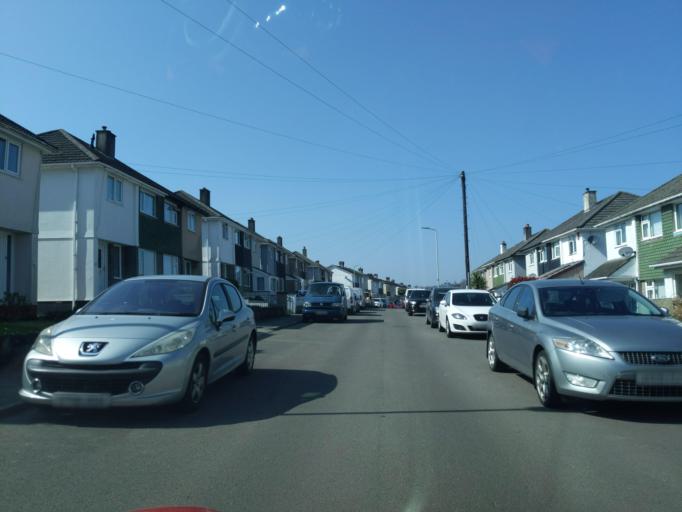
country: GB
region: England
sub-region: Devon
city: Plympton
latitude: 50.3872
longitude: -4.0692
